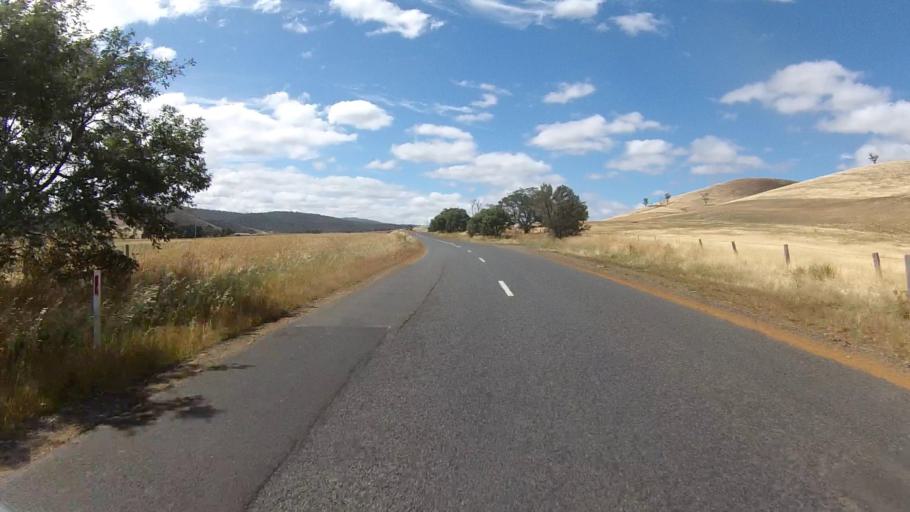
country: AU
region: Tasmania
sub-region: Brighton
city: Bridgewater
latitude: -42.5533
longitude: 147.3814
